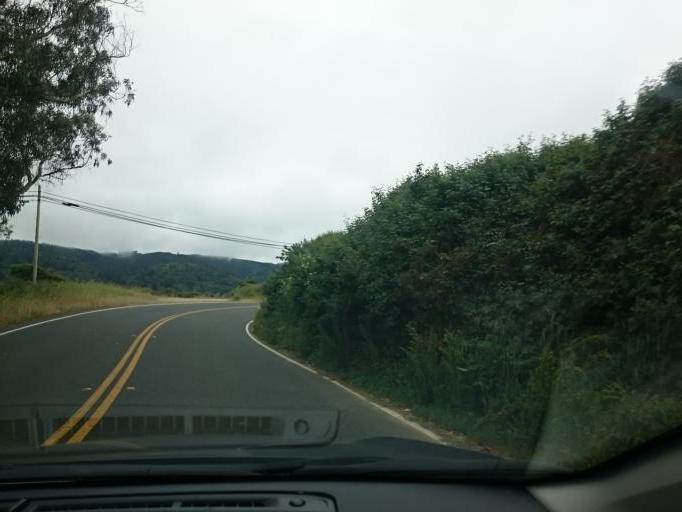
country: US
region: California
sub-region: Marin County
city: Inverness
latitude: 38.0925
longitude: -122.8261
